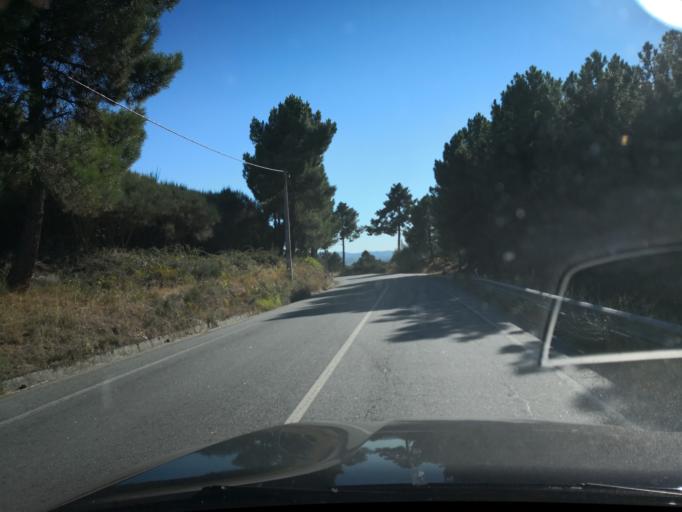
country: PT
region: Vila Real
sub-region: Valpacos
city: Valpacos
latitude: 41.6353
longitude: -7.3175
